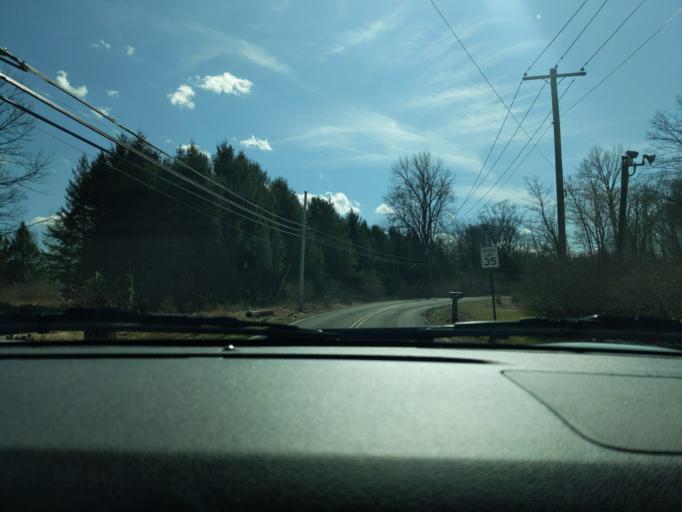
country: US
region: Pennsylvania
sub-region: Bucks County
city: Richlandtown
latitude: 40.4610
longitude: -75.2701
